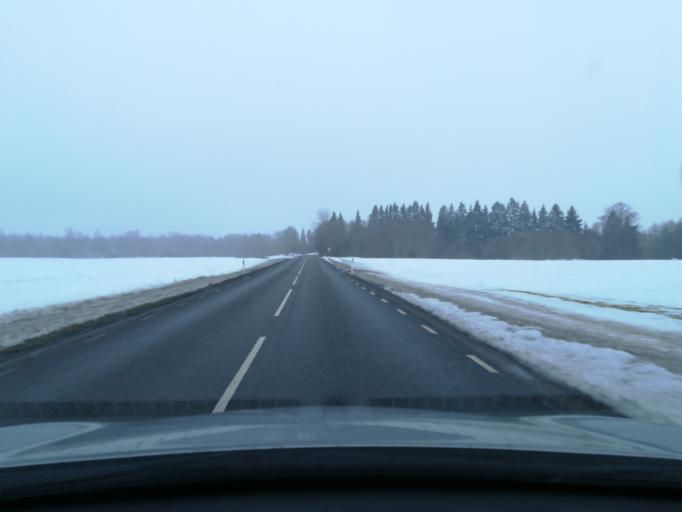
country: EE
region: Harju
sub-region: Raasiku vald
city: Arukula
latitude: 59.3486
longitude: 25.1259
